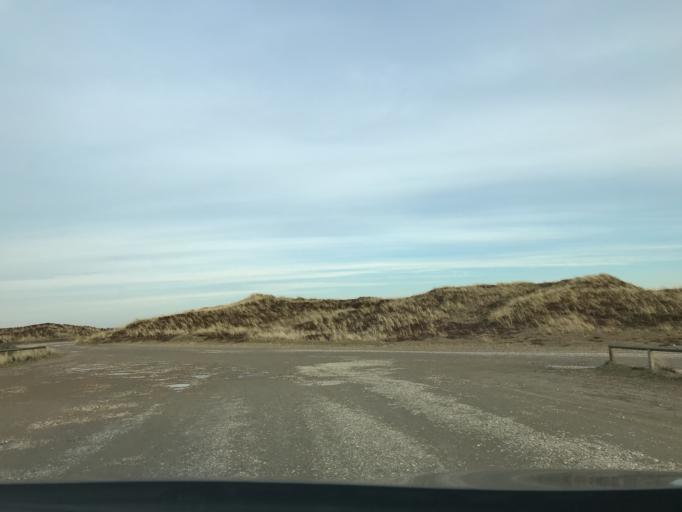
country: DK
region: Central Jutland
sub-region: Ringkobing-Skjern Kommune
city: Hvide Sande
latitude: 55.8171
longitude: 8.1774
